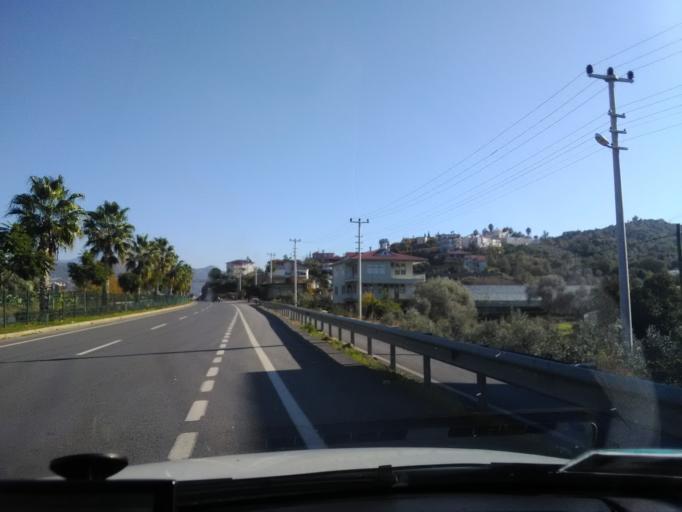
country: TR
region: Antalya
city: Gazipasa
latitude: 36.2568
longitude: 32.3271
